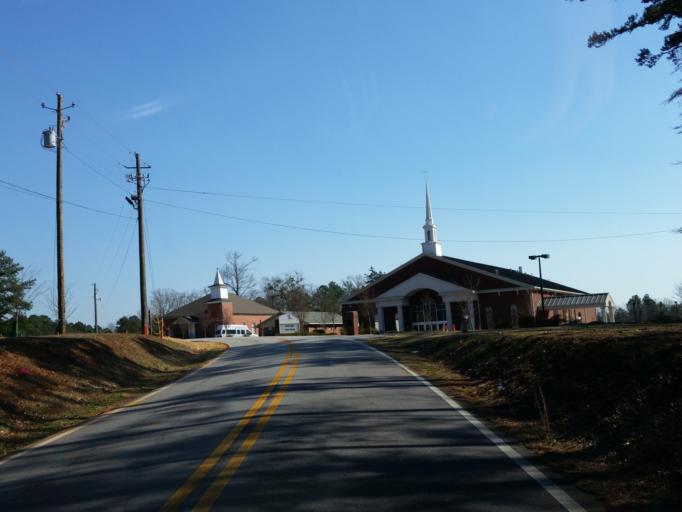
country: US
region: Georgia
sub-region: Henry County
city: Stockbridge
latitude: 33.4739
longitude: -84.2235
